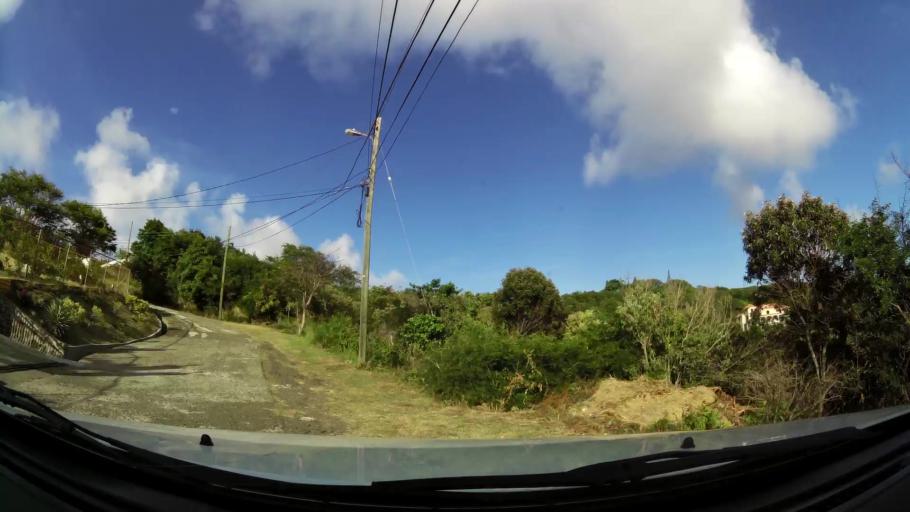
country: LC
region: Gros-Islet
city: Gros Islet
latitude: 14.1001
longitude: -60.9367
